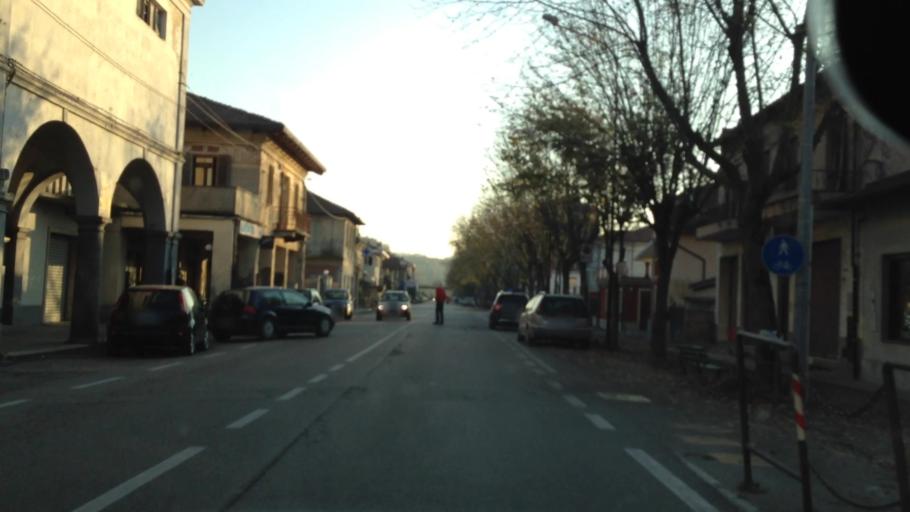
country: IT
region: Piedmont
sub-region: Provincia di Vercelli
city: Crescentino
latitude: 45.1899
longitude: 8.1021
